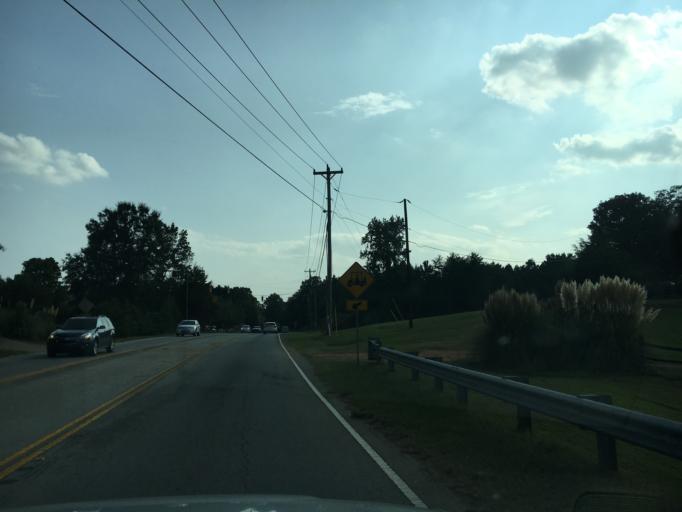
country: US
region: South Carolina
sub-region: Greenville County
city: Wade Hampton
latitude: 34.9228
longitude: -82.3477
